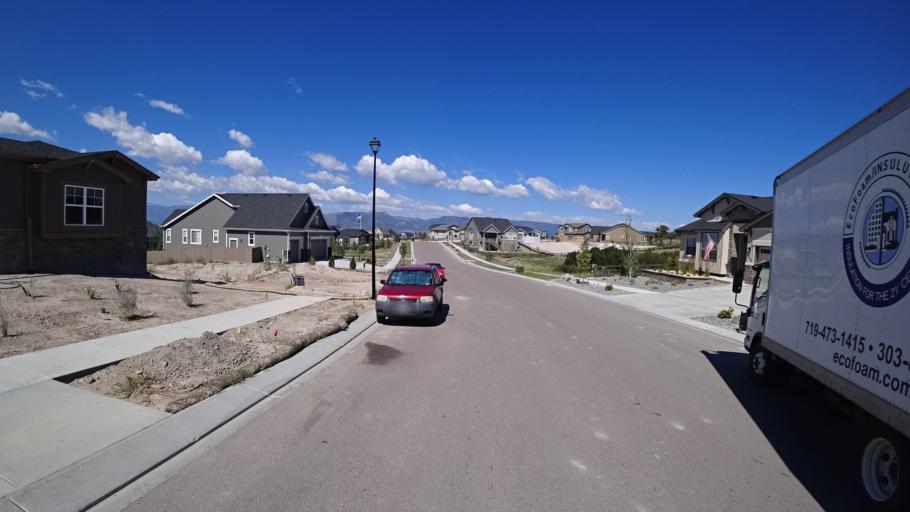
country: US
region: Colorado
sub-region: El Paso County
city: Black Forest
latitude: 38.9825
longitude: -104.7468
